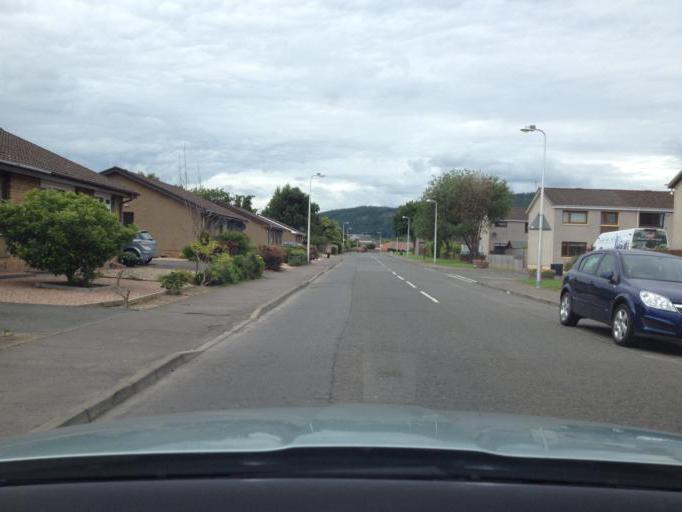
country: GB
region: Scotland
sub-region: Perth and Kinross
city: Bridge of Earn
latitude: 56.3429
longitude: -3.4026
